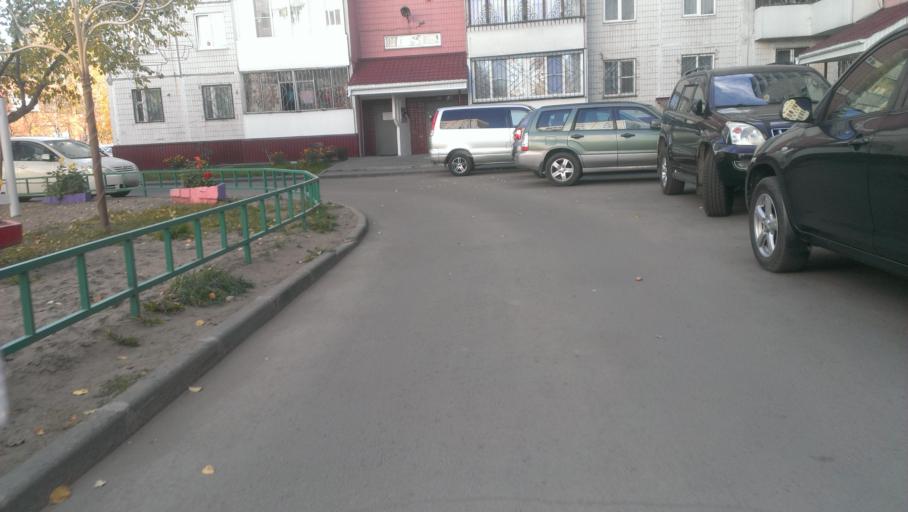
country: RU
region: Altai Krai
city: Novosilikatnyy
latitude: 53.3341
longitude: 83.6777
